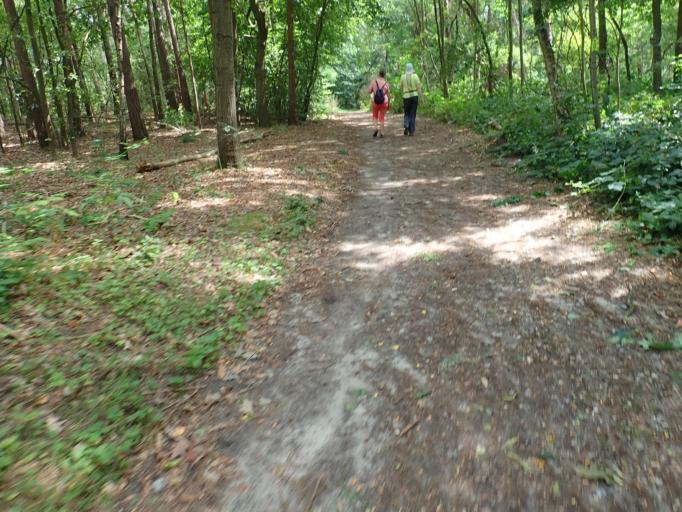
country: BE
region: Flanders
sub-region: Provincie Vlaams-Brabant
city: Keerbergen
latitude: 50.9966
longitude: 4.6184
